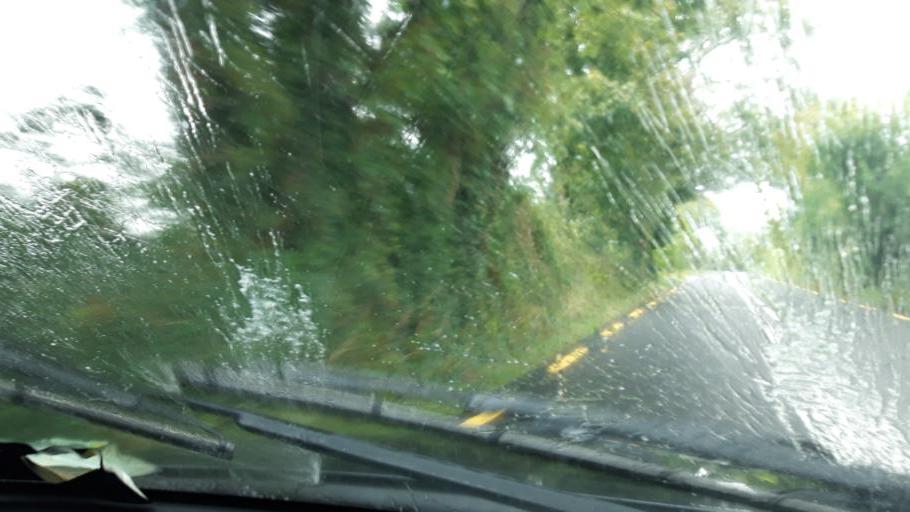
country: IE
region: Leinster
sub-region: Loch Garman
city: New Ross
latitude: 52.4282
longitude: -6.8274
